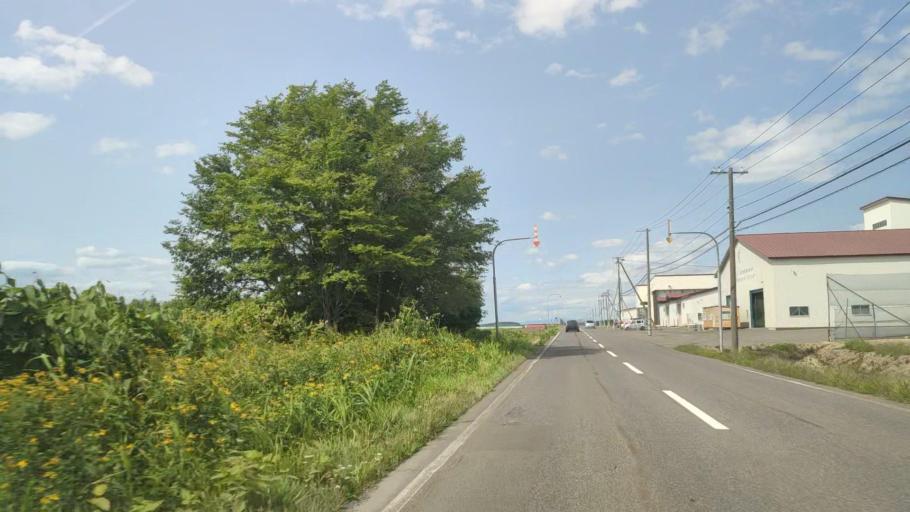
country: JP
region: Hokkaido
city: Nayoro
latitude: 44.2036
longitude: 142.4158
